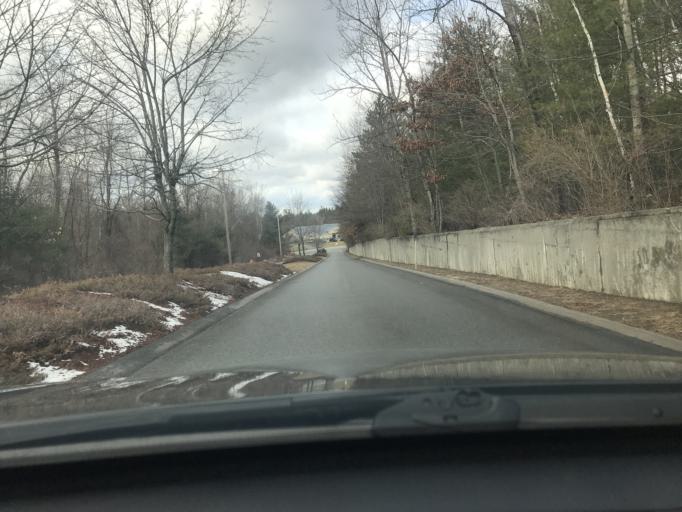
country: US
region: Massachusetts
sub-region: Middlesex County
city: Tyngsboro
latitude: 42.6594
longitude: -71.4252
